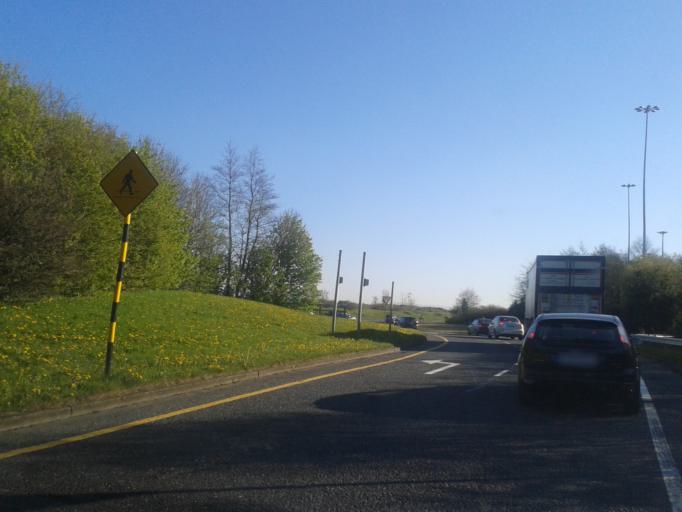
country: IE
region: Leinster
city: Beaumont
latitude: 53.3981
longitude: -6.2373
